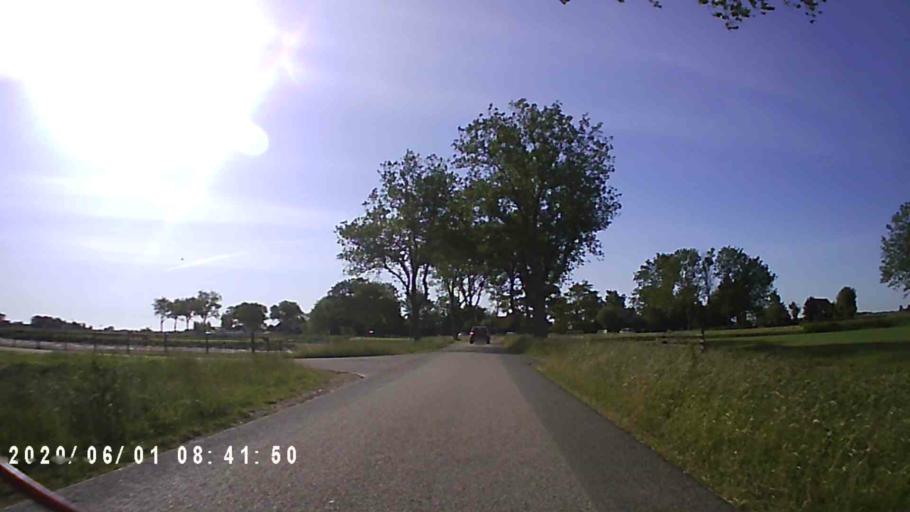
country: NL
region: Friesland
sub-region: Gemeente Ferwerderadiel
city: Burdaard
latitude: 53.2867
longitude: 5.8461
